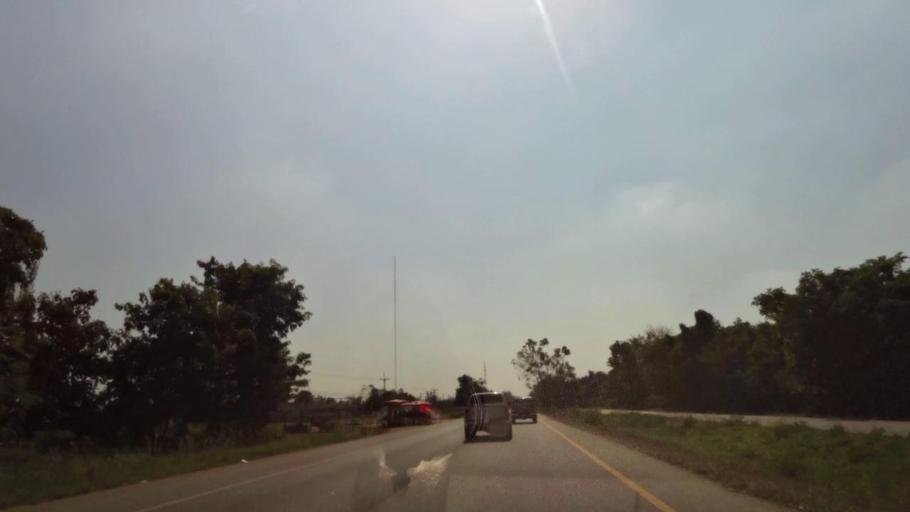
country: TH
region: Phichit
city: Wachira Barami
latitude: 16.4187
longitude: 100.1439
